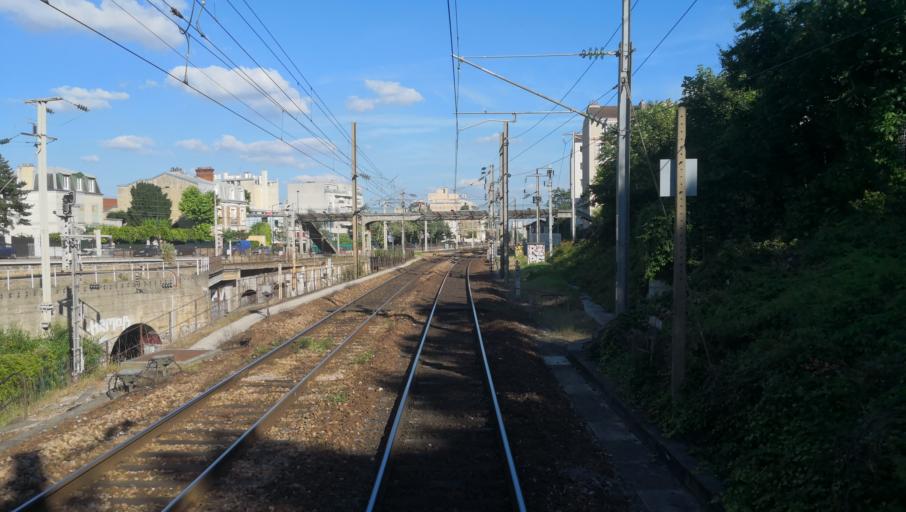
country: FR
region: Ile-de-France
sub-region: Departement des Hauts-de-Seine
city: Asnieres-sur-Seine
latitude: 48.9099
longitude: 2.2768
